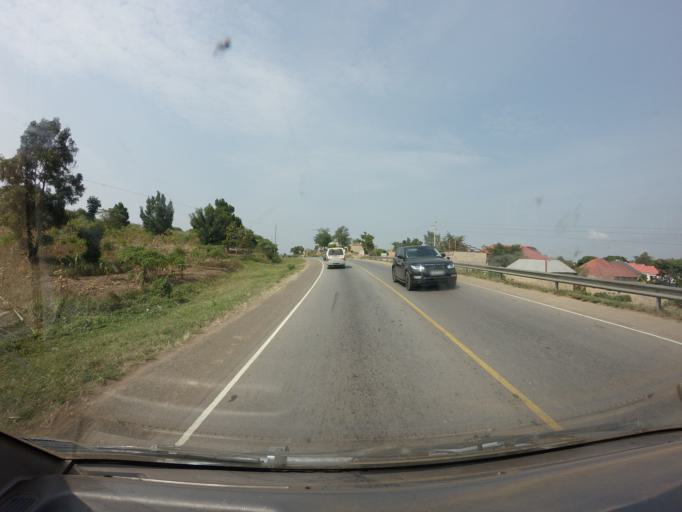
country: UG
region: Central Region
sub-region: Lwengo District
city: Lwengo
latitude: -0.3987
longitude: 31.4055
